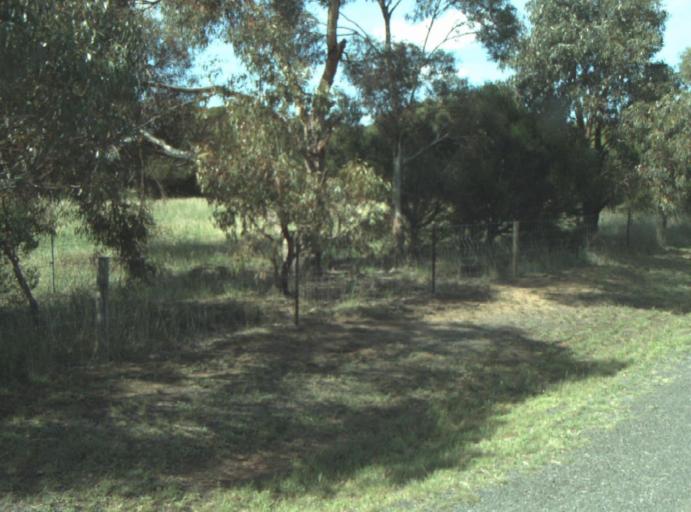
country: AU
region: Victoria
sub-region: Greater Geelong
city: Lara
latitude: -38.0111
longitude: 144.4164
